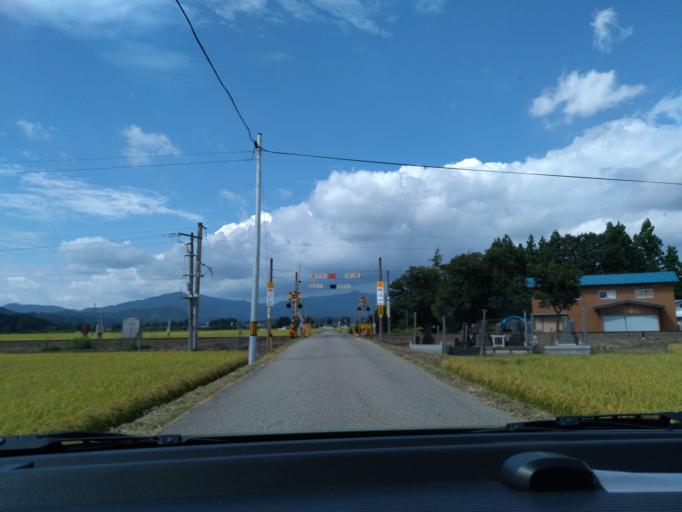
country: JP
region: Akita
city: Kakunodatemachi
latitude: 39.6043
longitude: 140.5865
